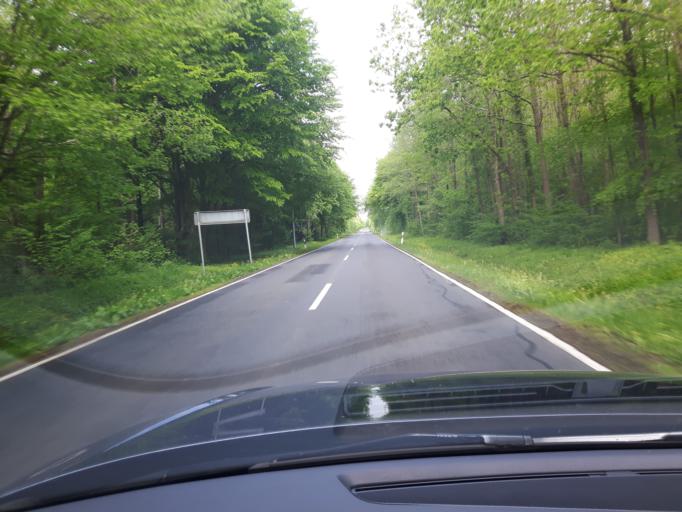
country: DE
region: Mecklenburg-Vorpommern
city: Velgast
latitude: 54.2311
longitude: 12.7292
